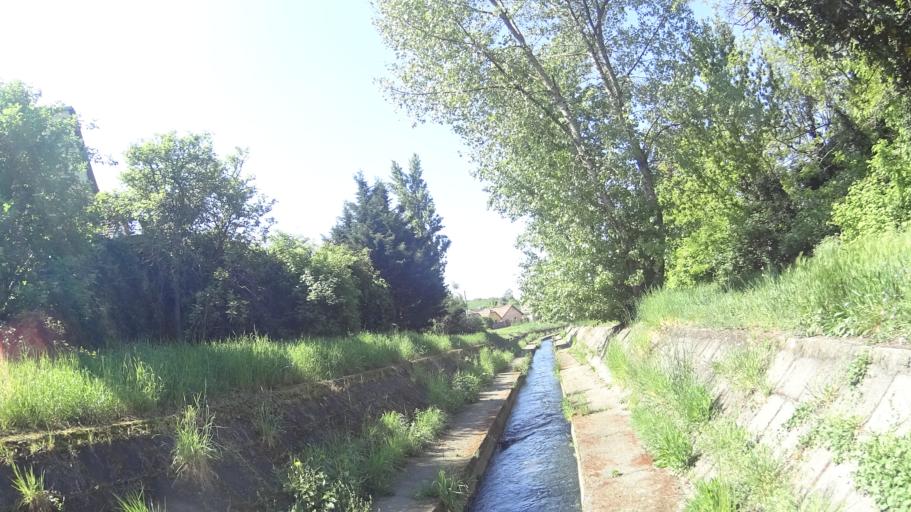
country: HU
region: Budapest
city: Budapest XXIII. keruelet
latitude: 47.3949
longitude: 19.1133
